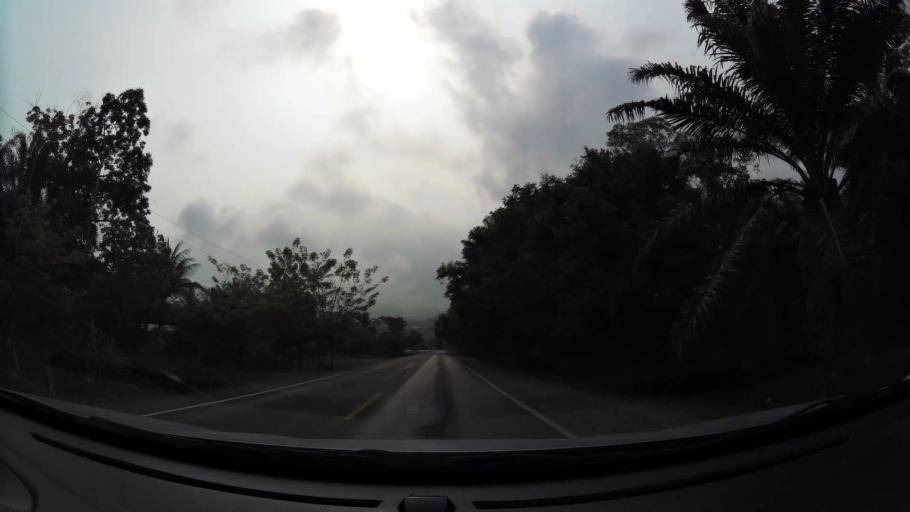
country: HN
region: Yoro
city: Toyos
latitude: 15.5545
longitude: -87.6327
